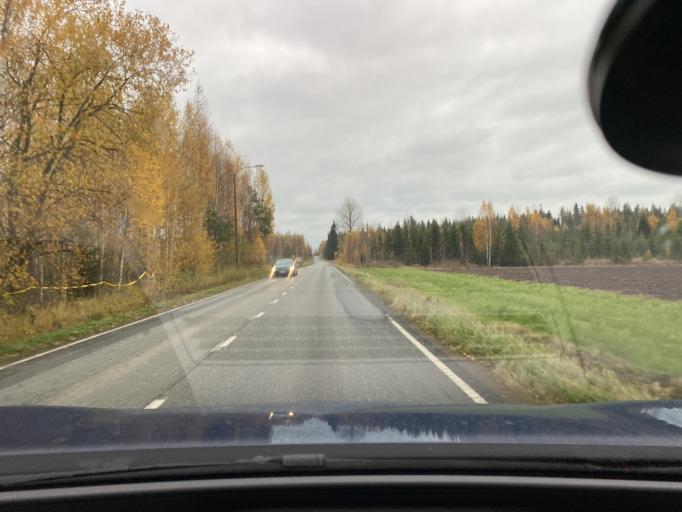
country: FI
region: Satakunta
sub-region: Pori
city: Vampula
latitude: 61.0737
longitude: 22.5293
